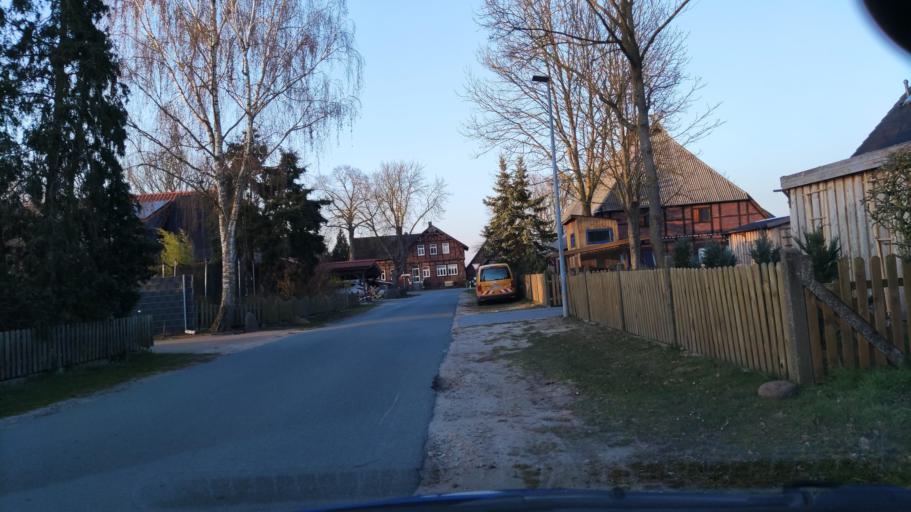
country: DE
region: Lower Saxony
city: Dannenberg
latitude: 53.1091
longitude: 11.1355
